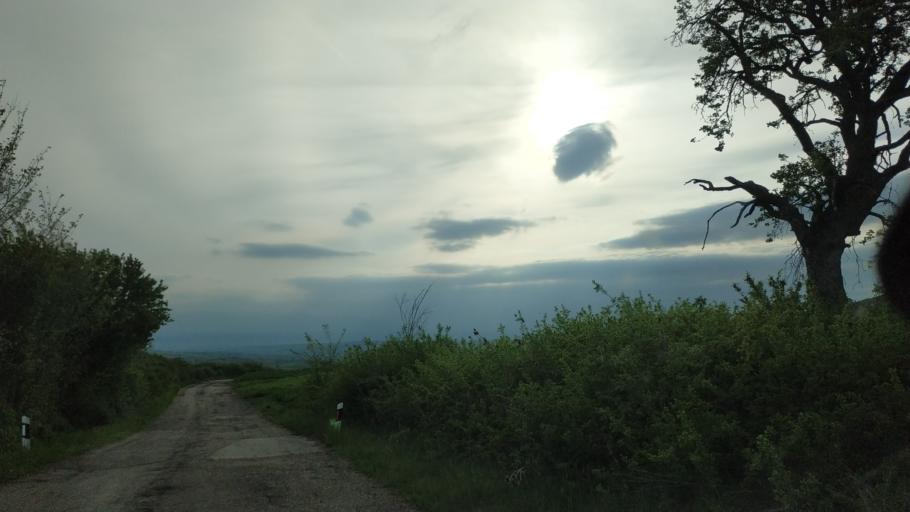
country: RS
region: Central Serbia
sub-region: Zajecarski Okrug
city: Soko Banja
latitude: 43.5269
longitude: 21.8752
